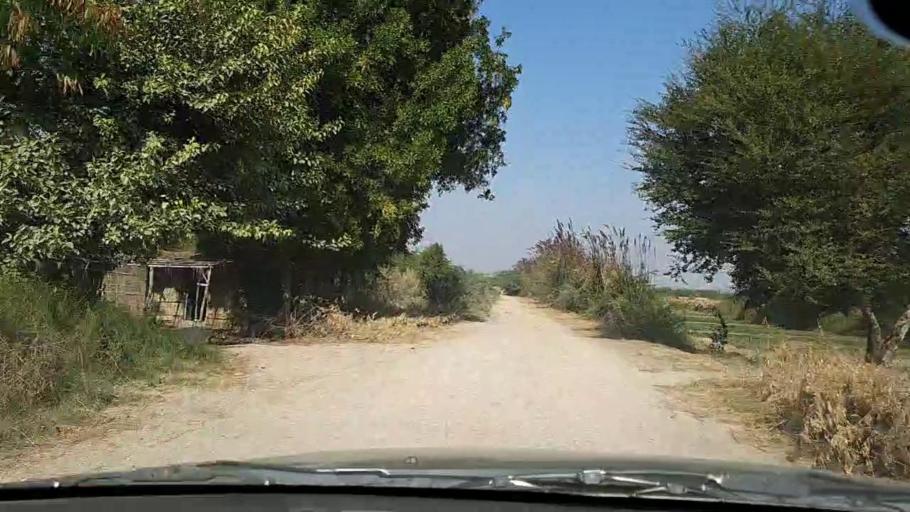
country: PK
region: Sindh
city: Chuhar Jamali
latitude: 24.4296
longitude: 67.7991
